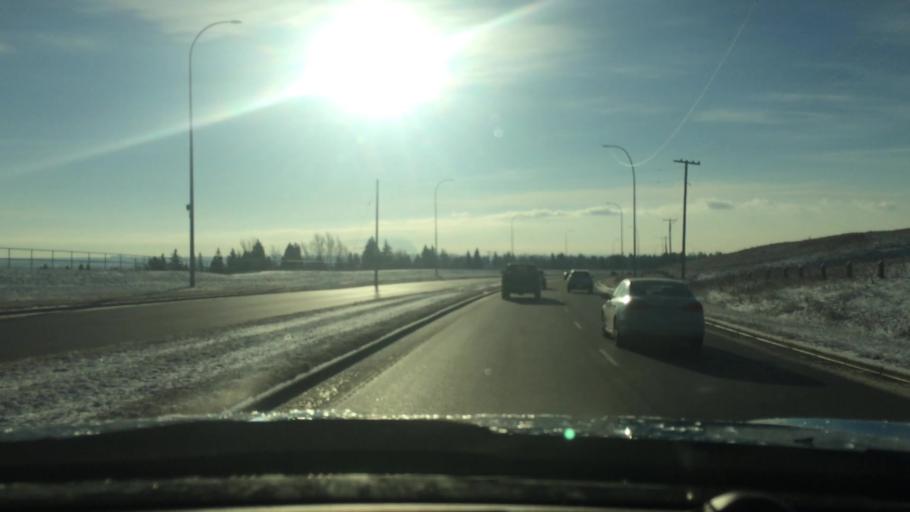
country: CA
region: Alberta
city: Calgary
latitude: 51.1169
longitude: -114.0860
